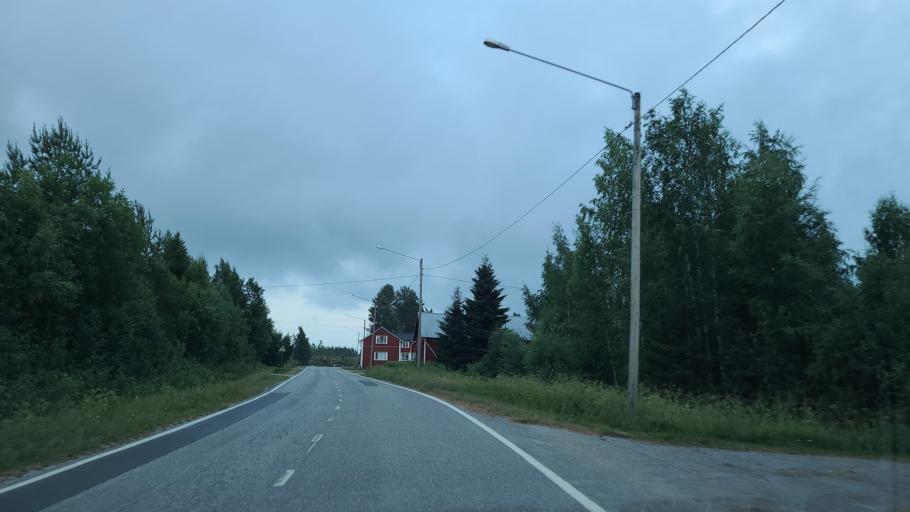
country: FI
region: Ostrobothnia
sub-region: Vaasa
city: Replot
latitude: 63.2842
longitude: 21.1235
